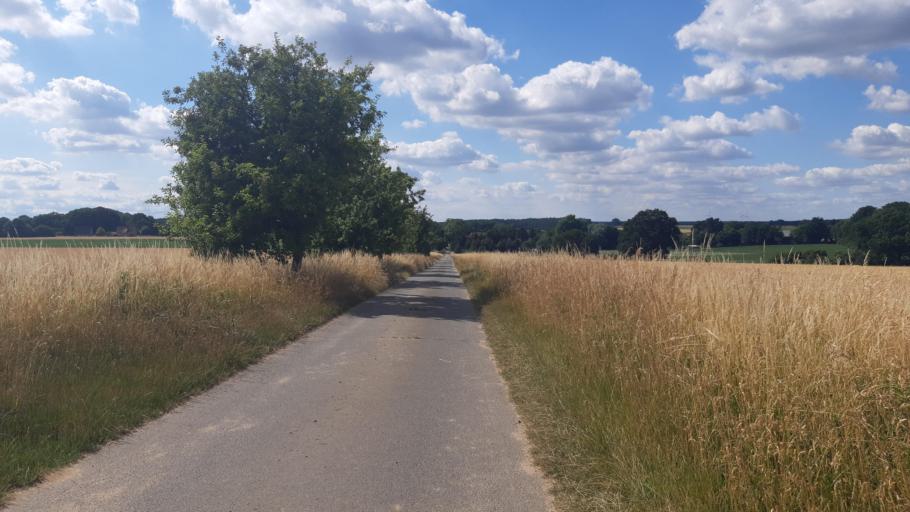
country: DE
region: Lower Saxony
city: Dahlem
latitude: 53.2097
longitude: 10.7684
